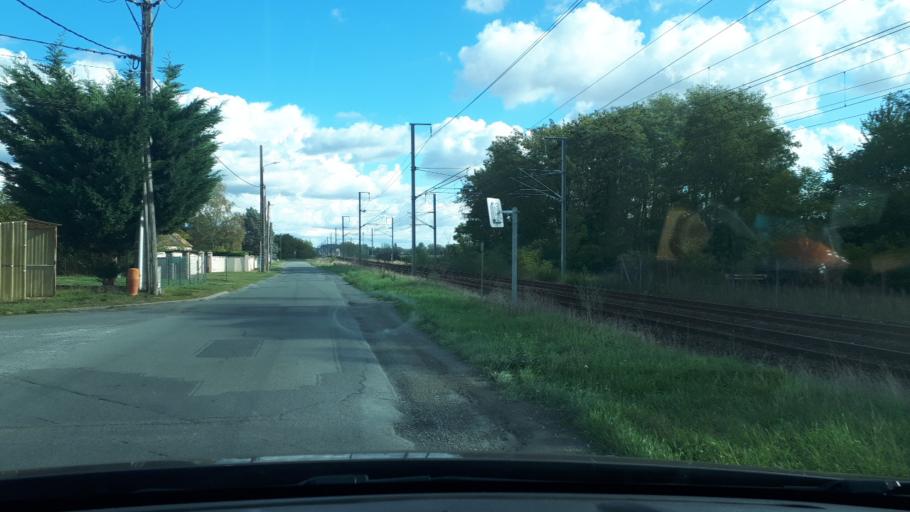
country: FR
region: Centre
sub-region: Departement du Loir-et-Cher
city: Saint-Aignan
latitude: 47.2943
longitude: 1.3678
